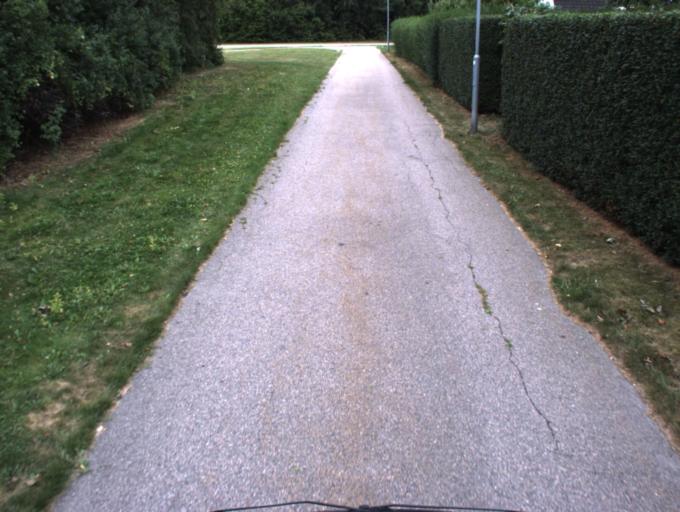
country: SE
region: Skane
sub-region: Helsingborg
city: Helsingborg
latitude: 56.0399
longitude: 12.7528
